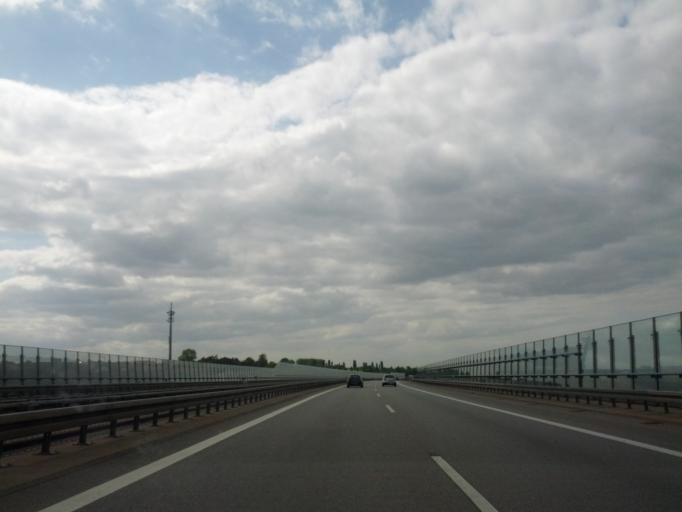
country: DE
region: Saxony
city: Kreischa
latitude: 50.9789
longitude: 13.7967
